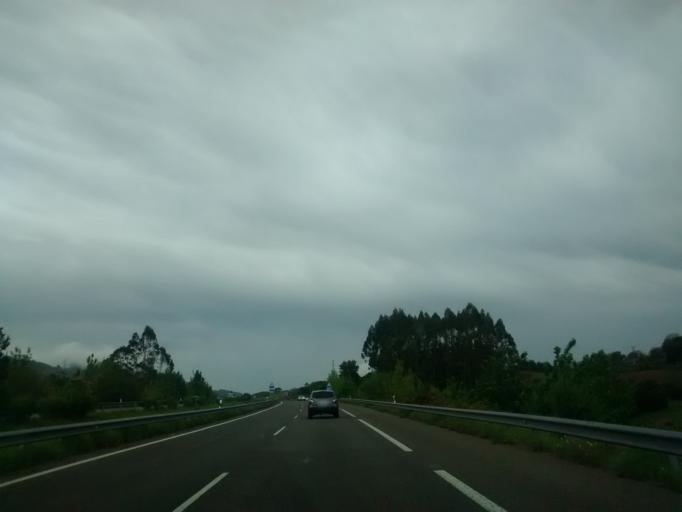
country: ES
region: Asturias
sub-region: Province of Asturias
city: Villaviciosa
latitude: 43.4745
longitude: -5.4638
